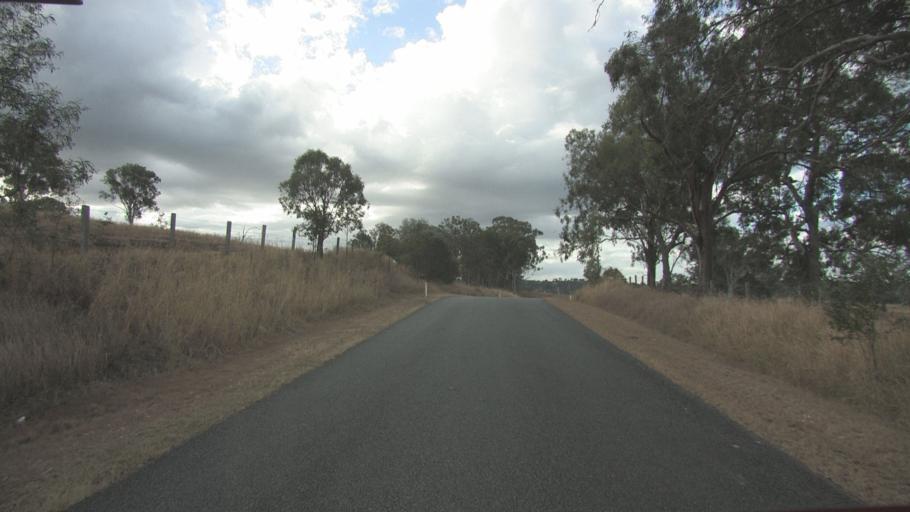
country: AU
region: Queensland
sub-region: Logan
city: Cedar Vale
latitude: -27.8920
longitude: 153.0657
